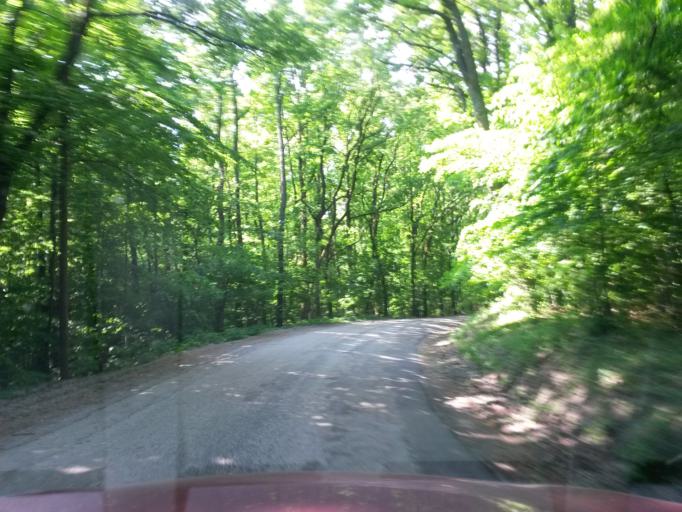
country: SK
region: Kosicky
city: Moldava nad Bodvou
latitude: 48.7190
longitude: 21.0318
